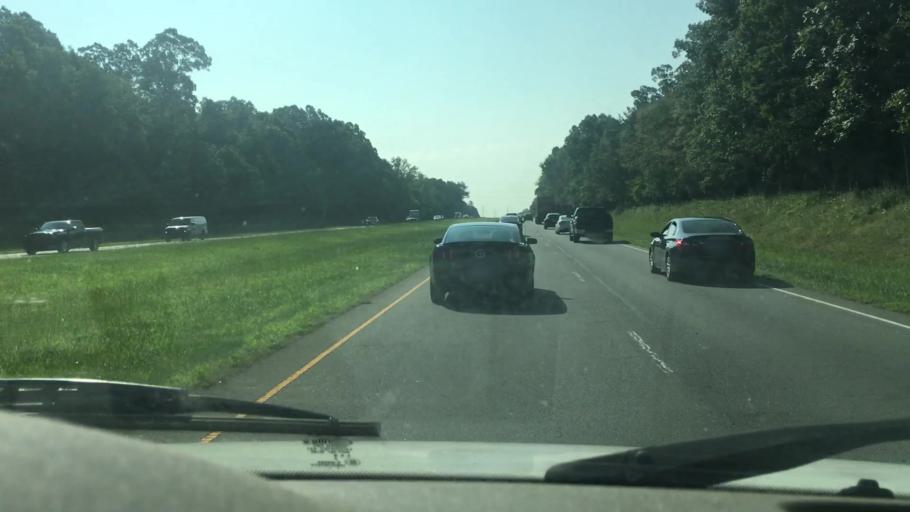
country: US
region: North Carolina
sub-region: Gaston County
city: Mount Holly
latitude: 35.3364
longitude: -80.9606
